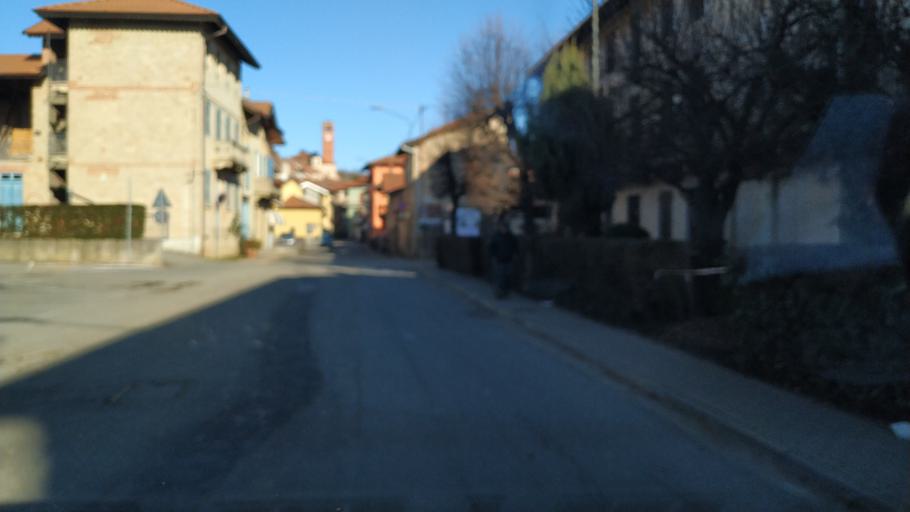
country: IT
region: Piedmont
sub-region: Provincia di Vercelli
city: Lozzolo
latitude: 45.6222
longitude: 8.3223
